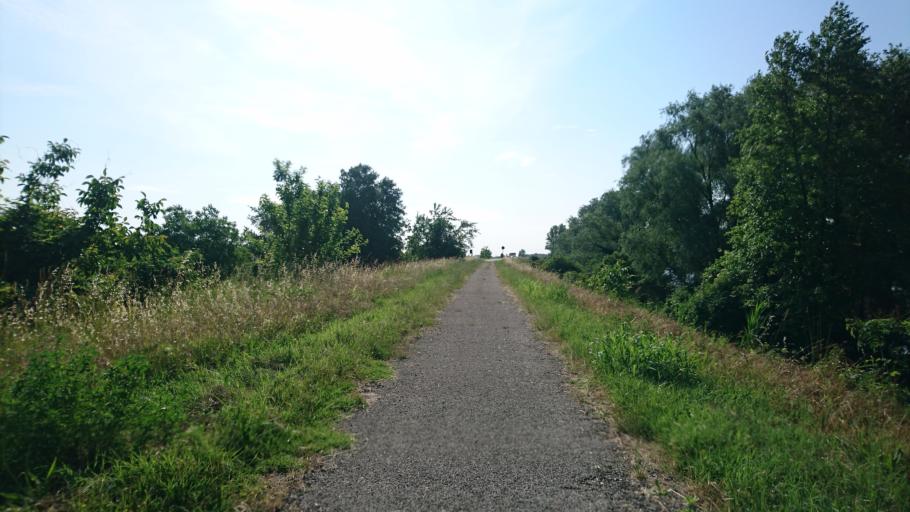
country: IT
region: Veneto
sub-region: Provincia di Verona
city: Villa Bartolomea
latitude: 45.1728
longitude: 11.3419
